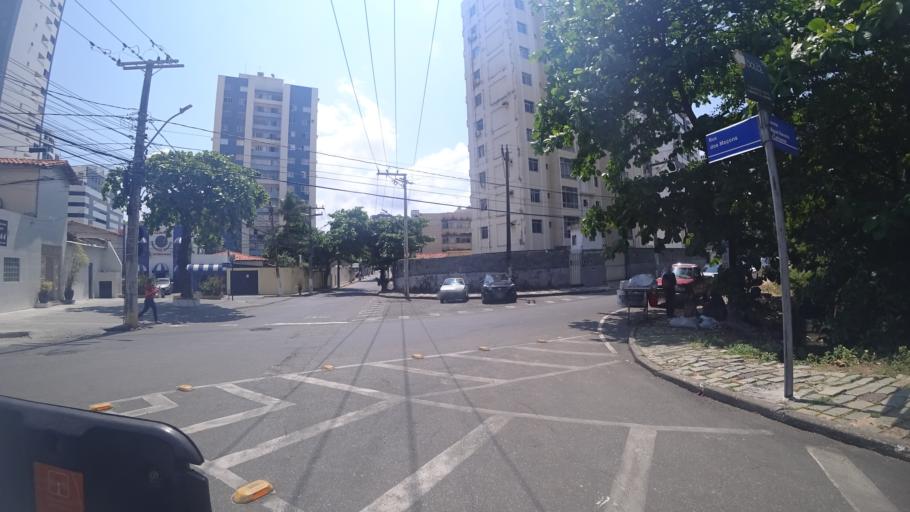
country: BR
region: Bahia
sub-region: Salvador
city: Salvador
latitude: -12.9945
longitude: -38.4530
